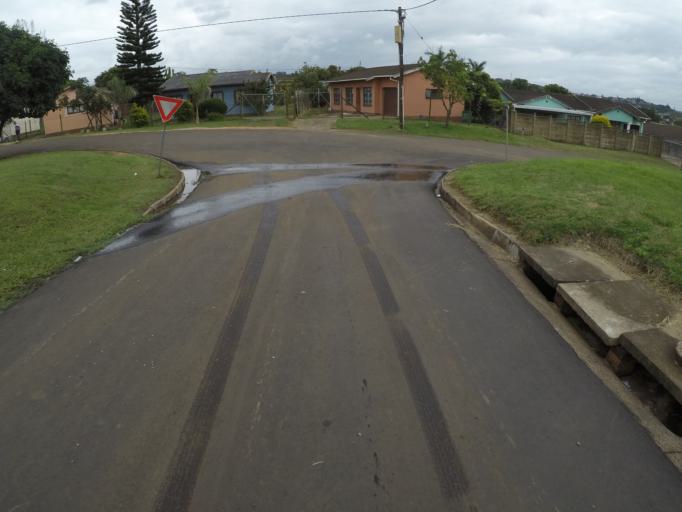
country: ZA
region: KwaZulu-Natal
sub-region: uThungulu District Municipality
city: Empangeni
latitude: -28.7828
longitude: 31.8514
